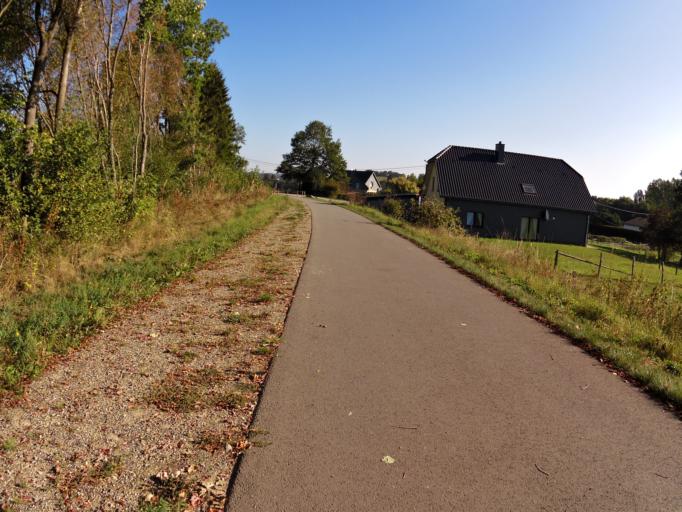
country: BE
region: Wallonia
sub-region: Province de Liege
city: Ambleve
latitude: 50.3369
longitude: 6.1191
